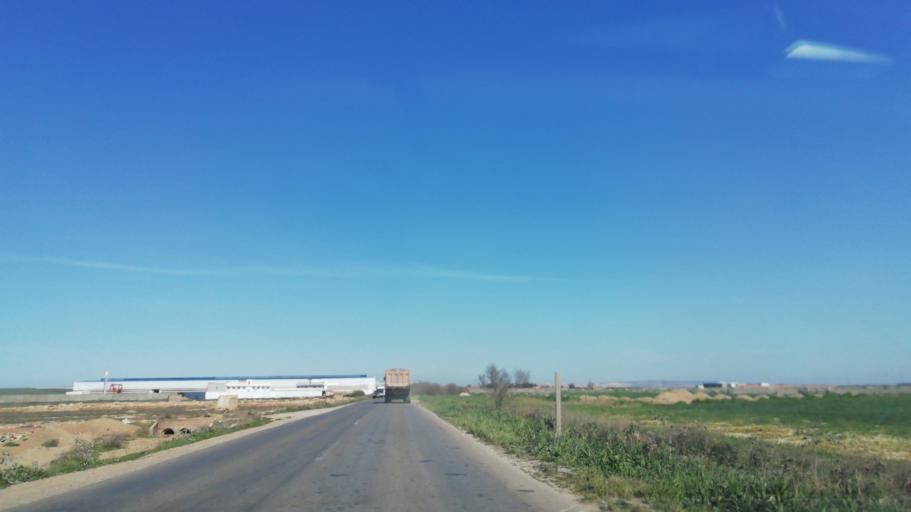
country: DZ
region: Oran
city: Es Senia
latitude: 35.5055
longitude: -0.5931
